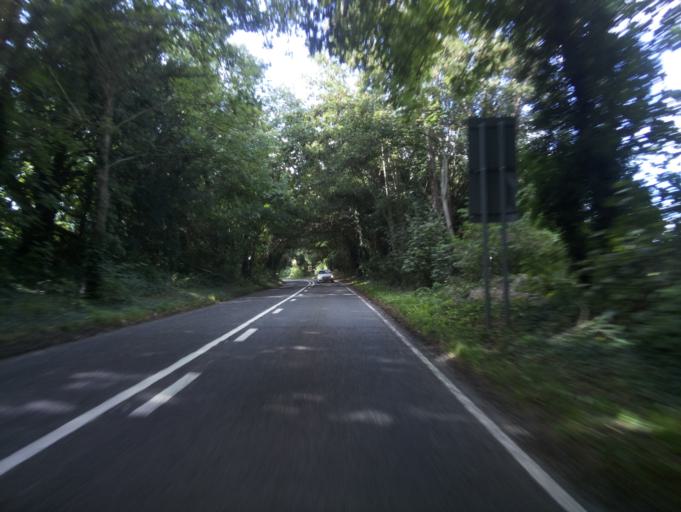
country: GB
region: England
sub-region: Hampshire
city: Abbotts Ann
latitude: 51.1127
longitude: -1.5660
